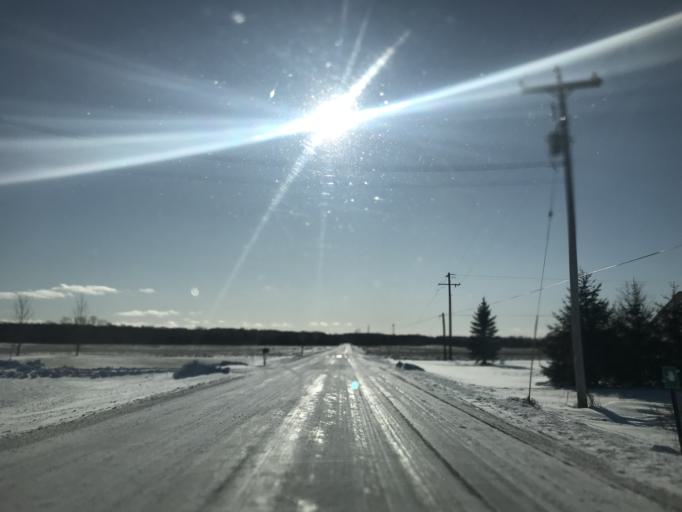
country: US
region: Wisconsin
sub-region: Door County
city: Sturgeon Bay
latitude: 44.8355
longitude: -87.5040
